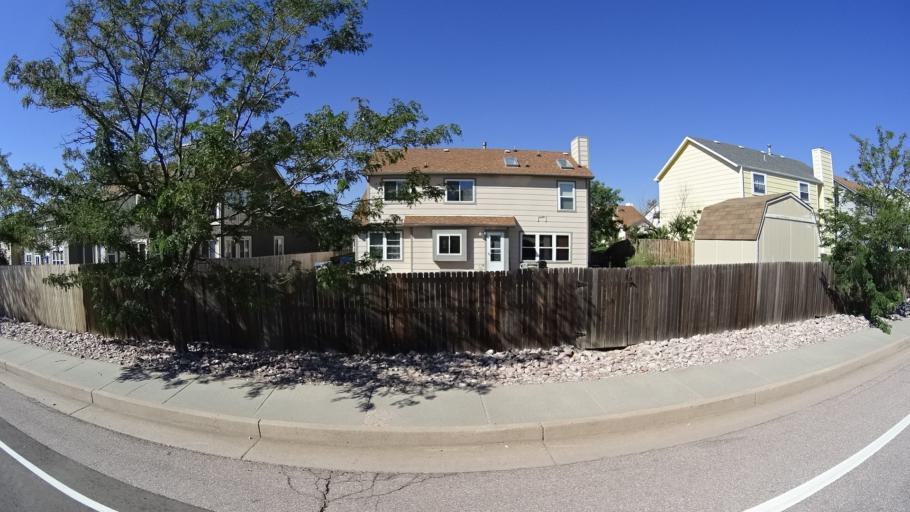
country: US
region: Colorado
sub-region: El Paso County
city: Black Forest
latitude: 38.9593
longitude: -104.7389
